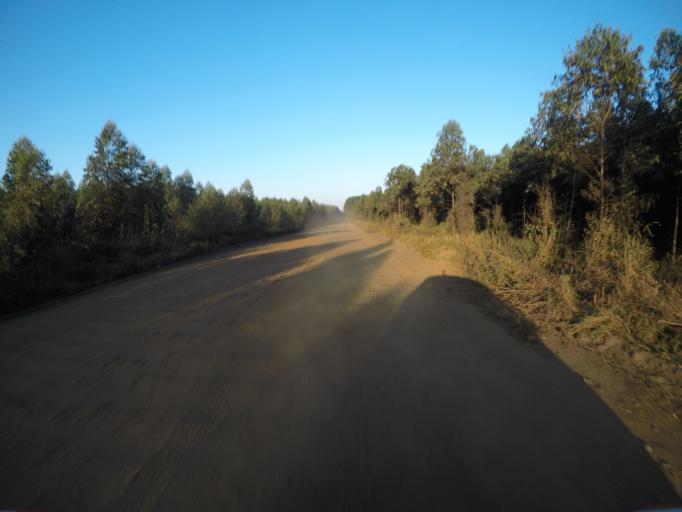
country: ZA
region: KwaZulu-Natal
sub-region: uThungulu District Municipality
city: KwaMbonambi
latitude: -28.6687
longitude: 32.0759
